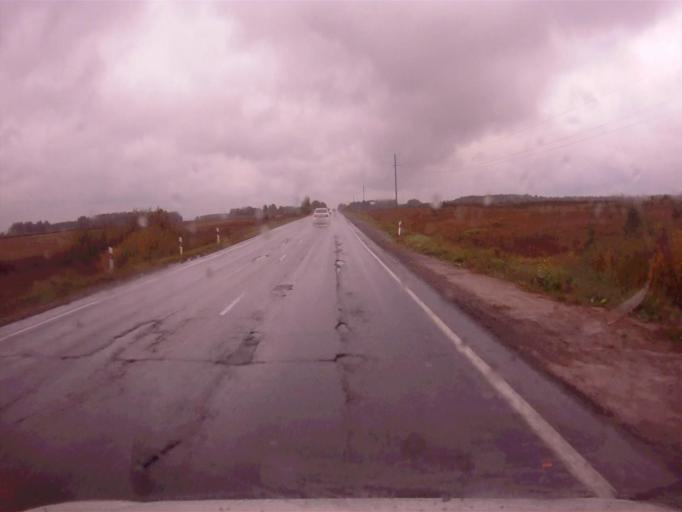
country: RU
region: Chelyabinsk
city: Novogornyy
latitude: 55.4880
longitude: 60.7113
